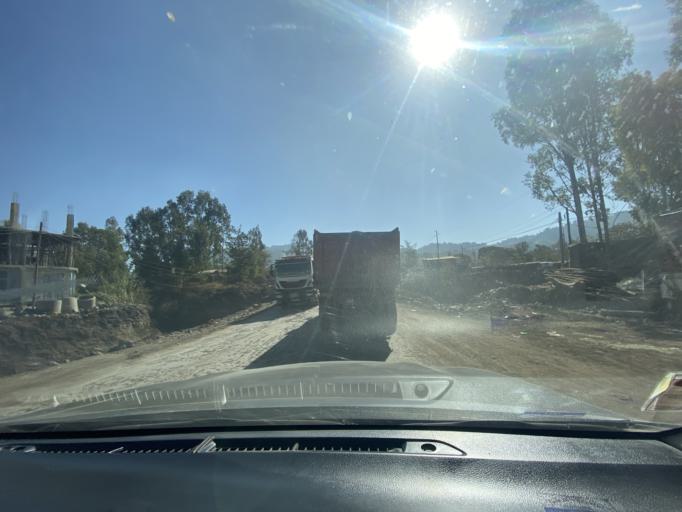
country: ET
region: Amhara
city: Robit
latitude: 11.8251
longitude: 39.5899
